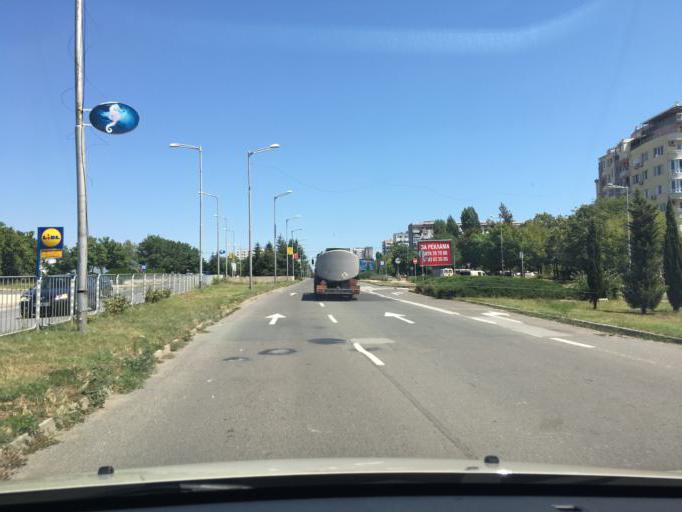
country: BG
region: Burgas
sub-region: Obshtina Burgas
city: Burgas
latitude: 42.5224
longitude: 27.4435
